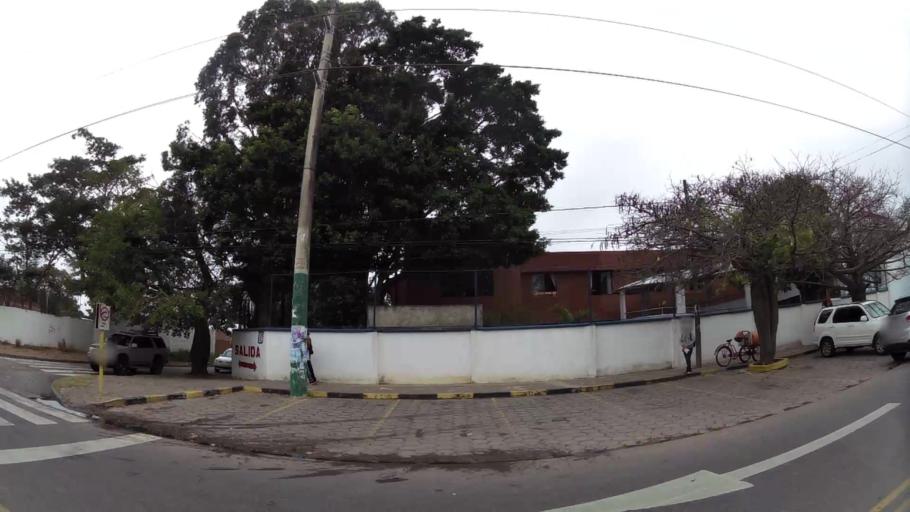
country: BO
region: Santa Cruz
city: Santa Cruz de la Sierra
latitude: -17.8064
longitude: -63.1694
